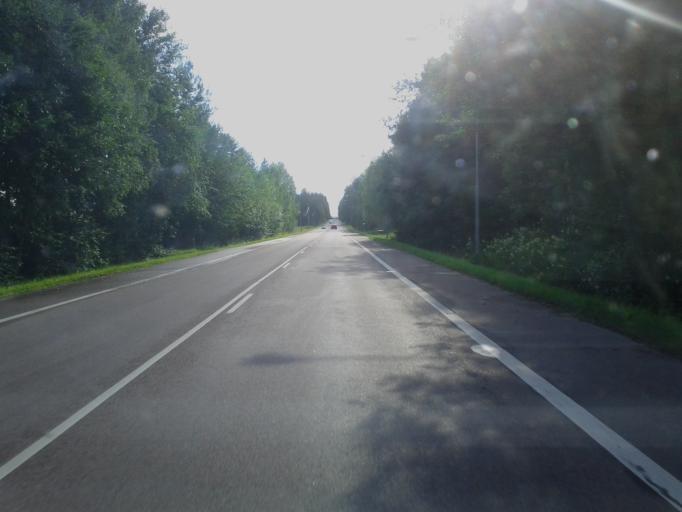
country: SE
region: Dalarna
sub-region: Borlange Kommun
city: Ornas
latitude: 60.5051
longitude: 15.5187
